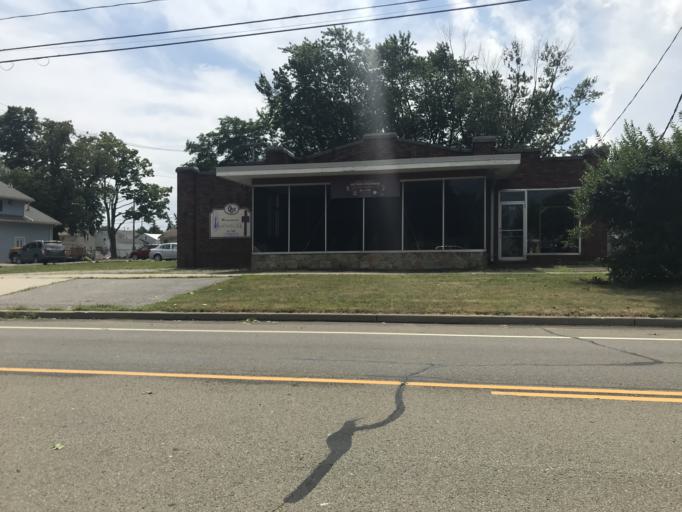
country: US
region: New York
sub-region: Chautauqua County
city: Dunkirk
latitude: 42.4867
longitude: -79.3394
